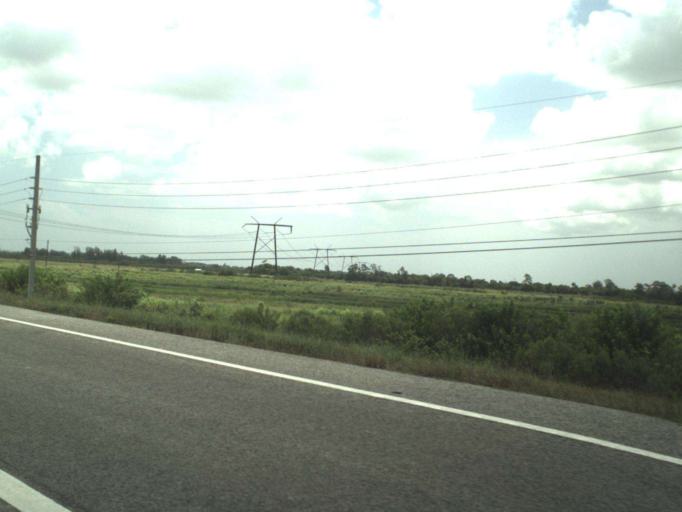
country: US
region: Florida
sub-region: Saint Lucie County
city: Fort Pierce South
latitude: 27.3806
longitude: -80.4718
